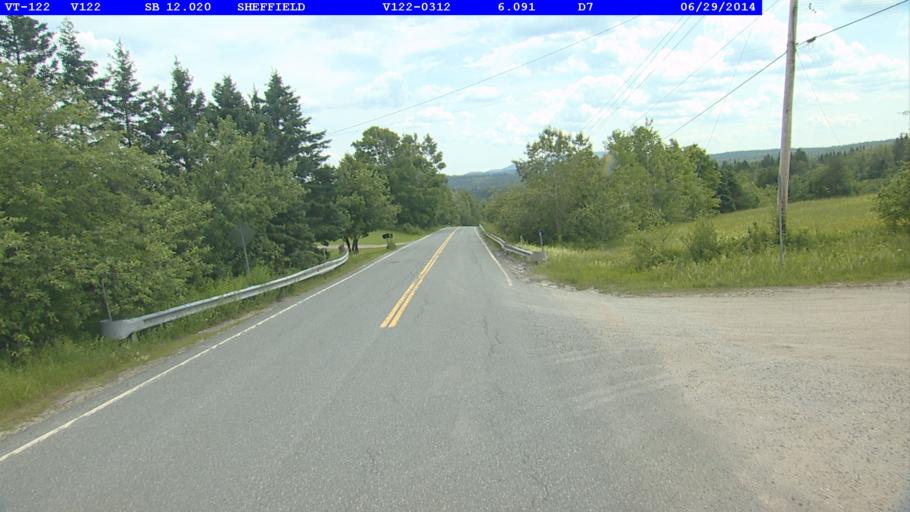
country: US
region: Vermont
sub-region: Caledonia County
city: Lyndonville
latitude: 44.6561
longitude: -72.1624
